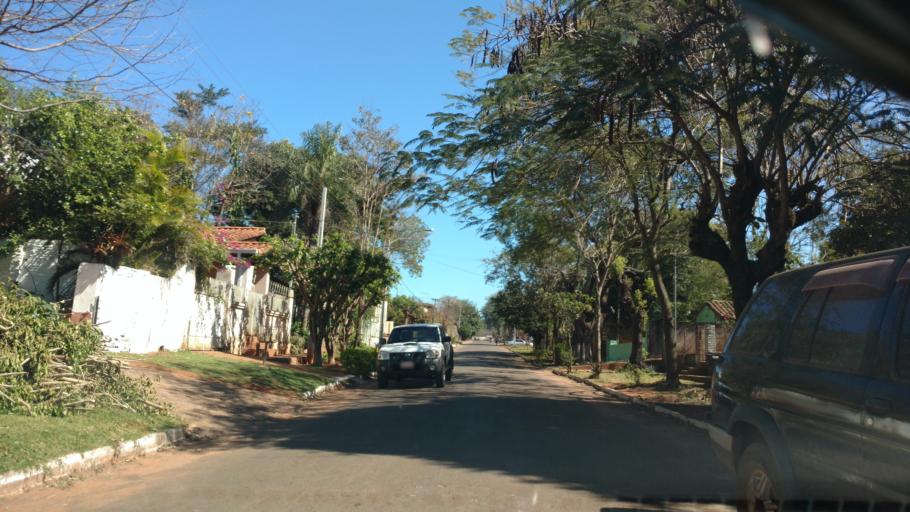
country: PY
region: Paraguari
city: Yaguaron
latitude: -25.5624
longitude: -57.2867
